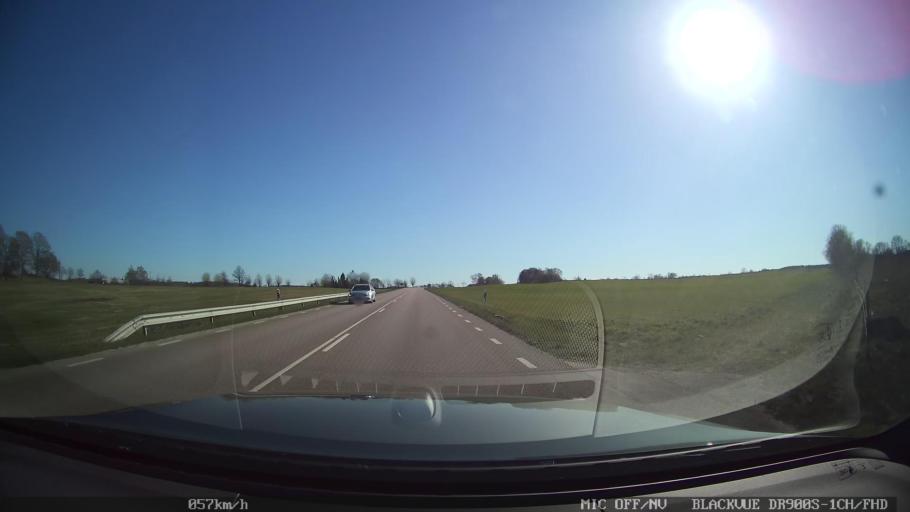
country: SE
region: Skane
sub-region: Klippans Kommun
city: Ljungbyhed
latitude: 55.9909
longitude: 13.2811
